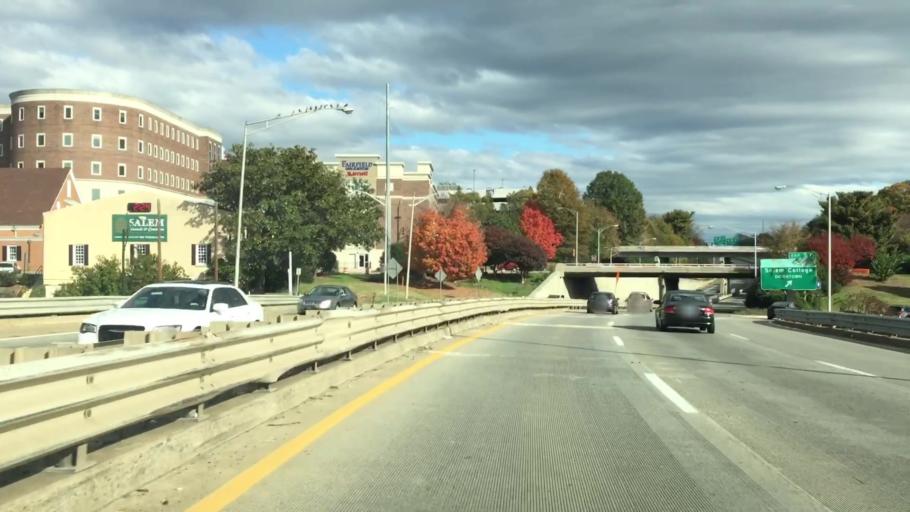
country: US
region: North Carolina
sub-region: Forsyth County
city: Winston-Salem
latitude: 36.0938
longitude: -80.2445
